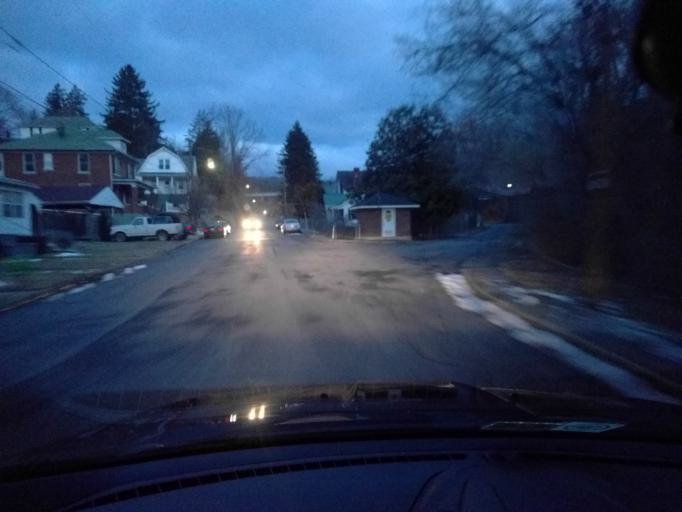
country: US
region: Virginia
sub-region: Alleghany County
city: Clifton Forge
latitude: 37.8230
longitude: -79.8266
